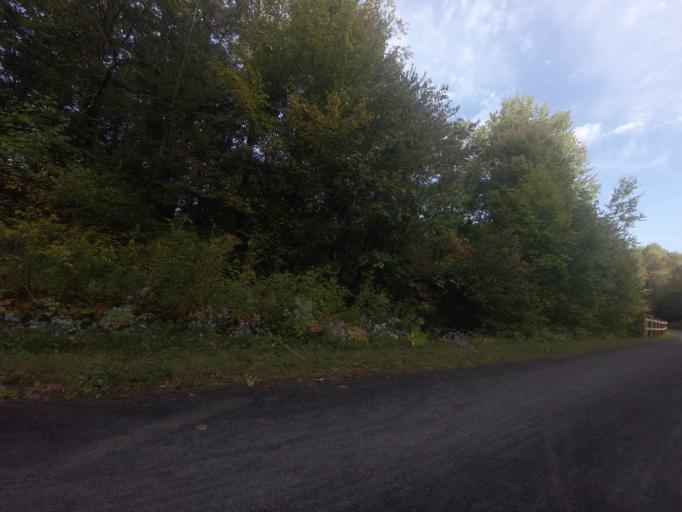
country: CA
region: Quebec
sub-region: Laurentides
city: Sainte-Adele
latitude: 45.9315
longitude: -74.1221
